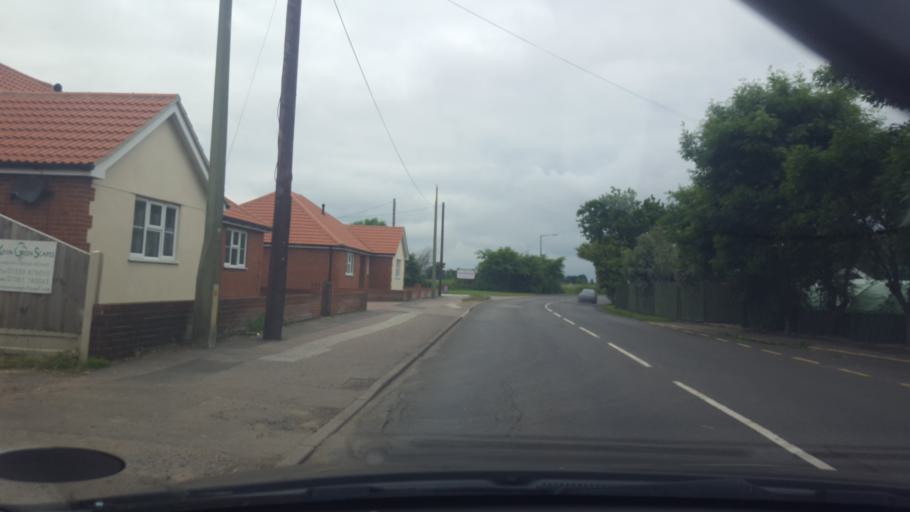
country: GB
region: England
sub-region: Essex
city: Clacton-on-Sea
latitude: 51.7894
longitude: 1.1191
